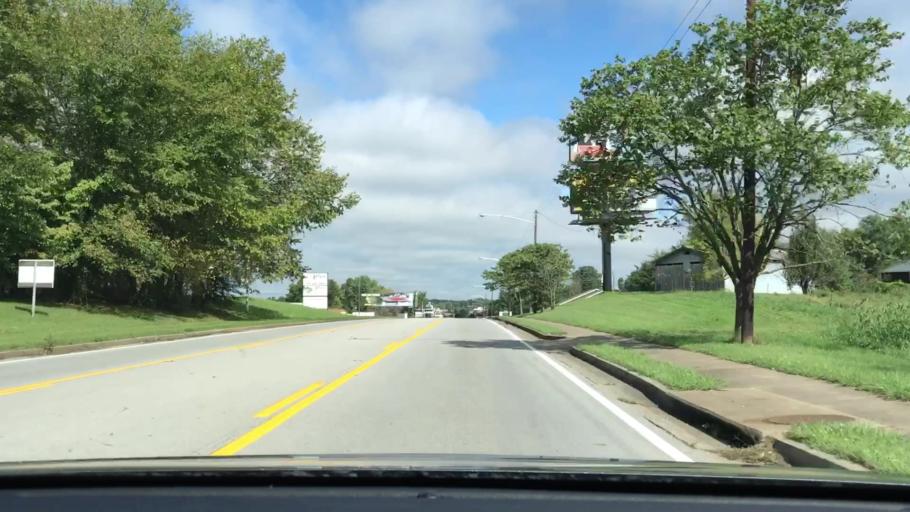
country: US
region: Kentucky
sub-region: Russell County
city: Jamestown
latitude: 37.0045
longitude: -85.0738
